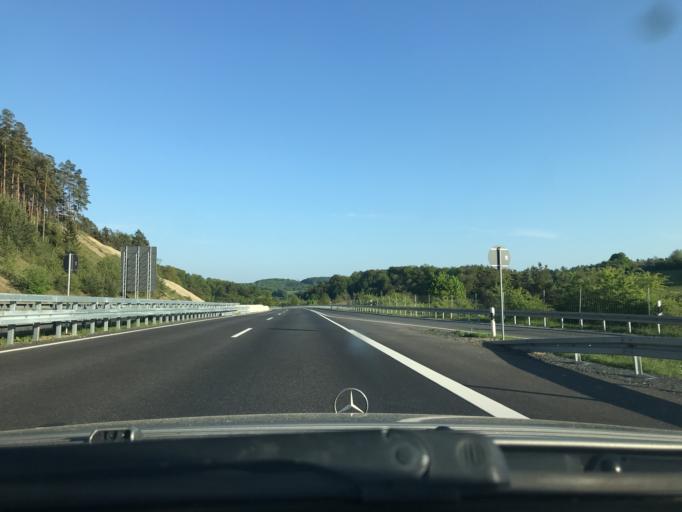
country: DE
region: Hesse
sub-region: Regierungsbezirk Kassel
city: Grossalmerode
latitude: 51.1895
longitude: 9.7930
